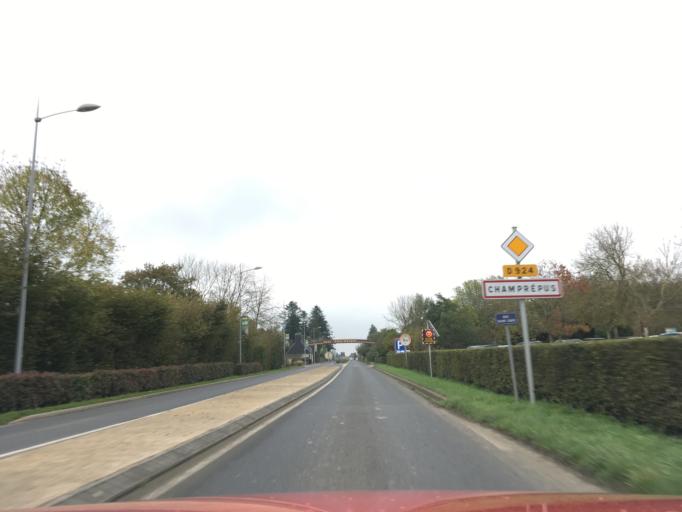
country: FR
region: Lower Normandy
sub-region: Departement de la Manche
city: La Haye-Pesnel
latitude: 48.8342
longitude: -1.3270
